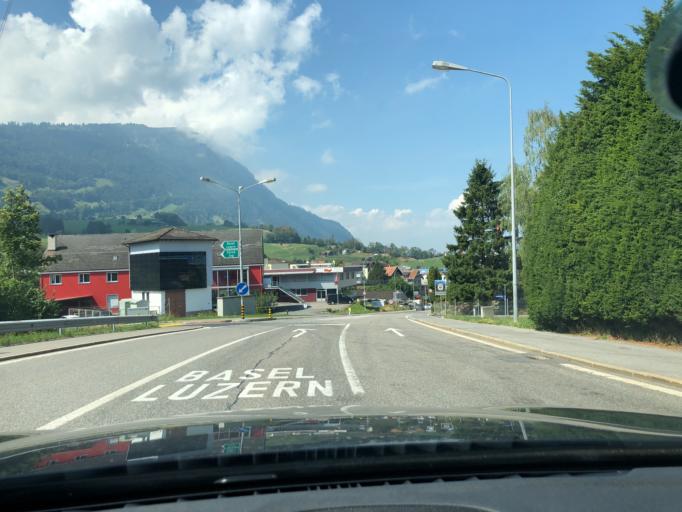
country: CH
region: Schwyz
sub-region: Bezirk Schwyz
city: Goldau
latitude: 47.0430
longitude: 8.5494
